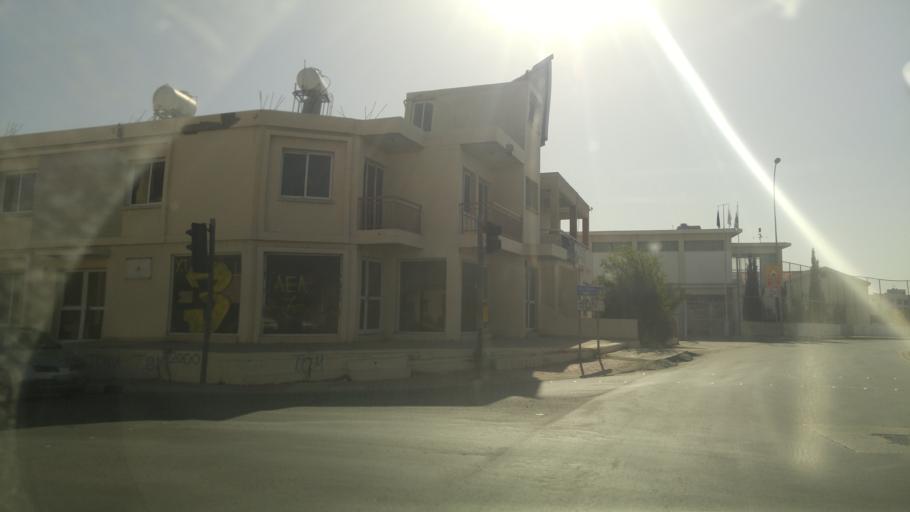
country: CY
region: Limassol
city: Limassol
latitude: 34.7027
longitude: 33.0478
